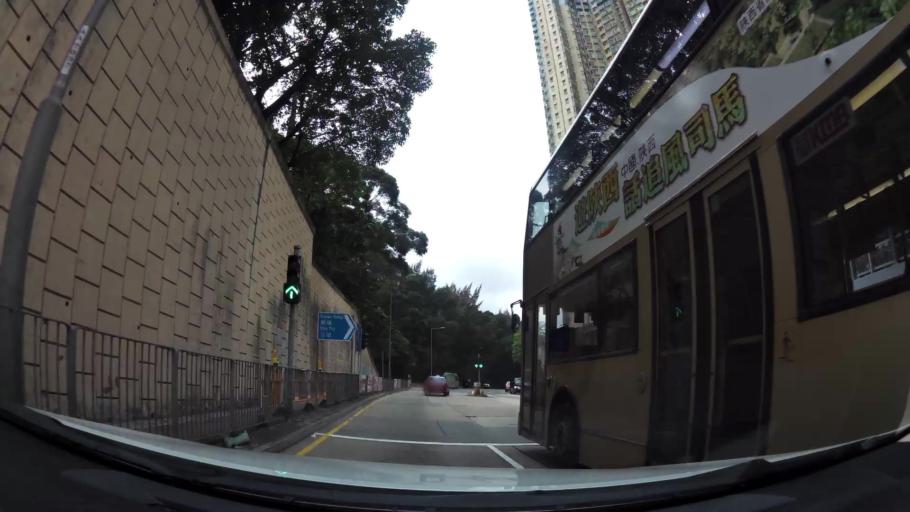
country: HK
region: Wong Tai Sin
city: Wong Tai Sin
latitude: 22.3427
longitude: 114.2017
